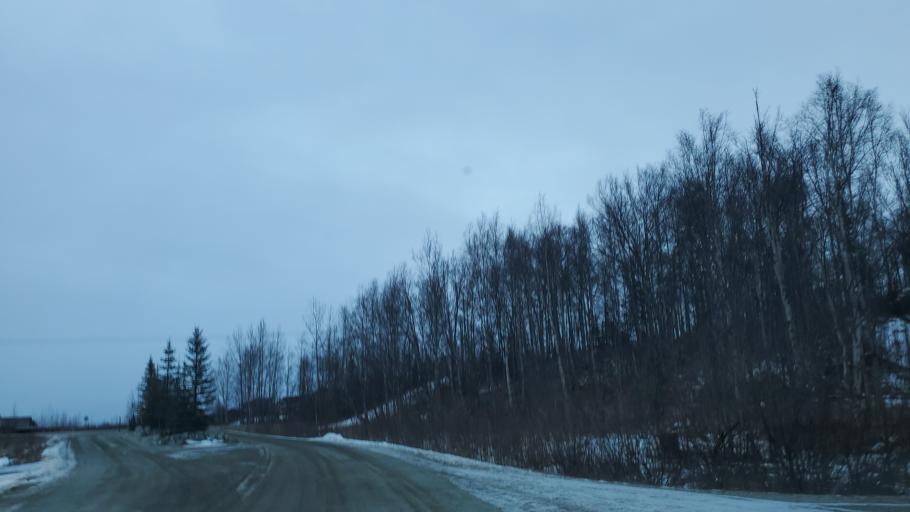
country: US
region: Alaska
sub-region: Matanuska-Susitna Borough
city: Farm Loop
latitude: 61.6524
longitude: -149.2174
